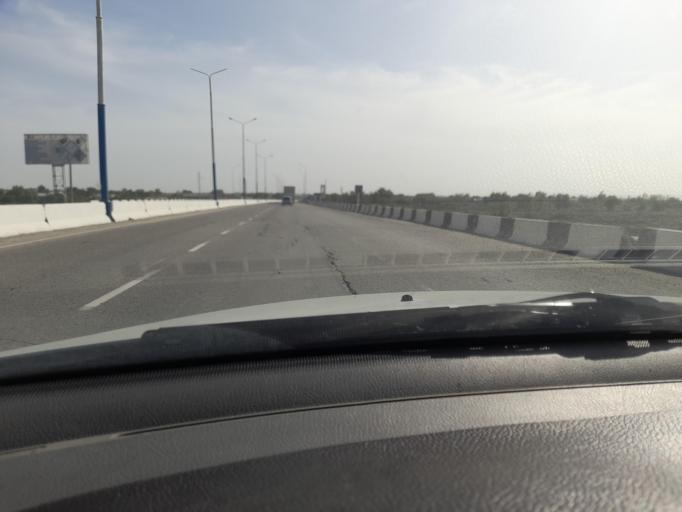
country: UZ
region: Samarqand
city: Kattaqo'rg'on
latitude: 39.9291
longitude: 66.3614
